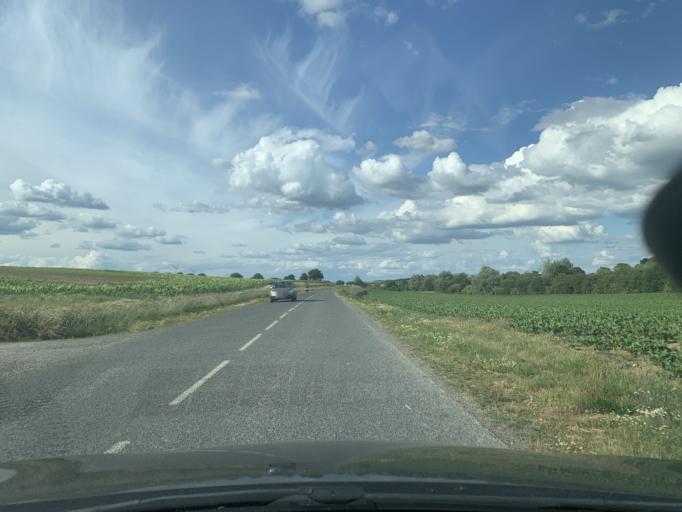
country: FR
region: Nord-Pas-de-Calais
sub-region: Departement du Nord
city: Gouzeaucourt
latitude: 50.0692
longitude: 3.1327
